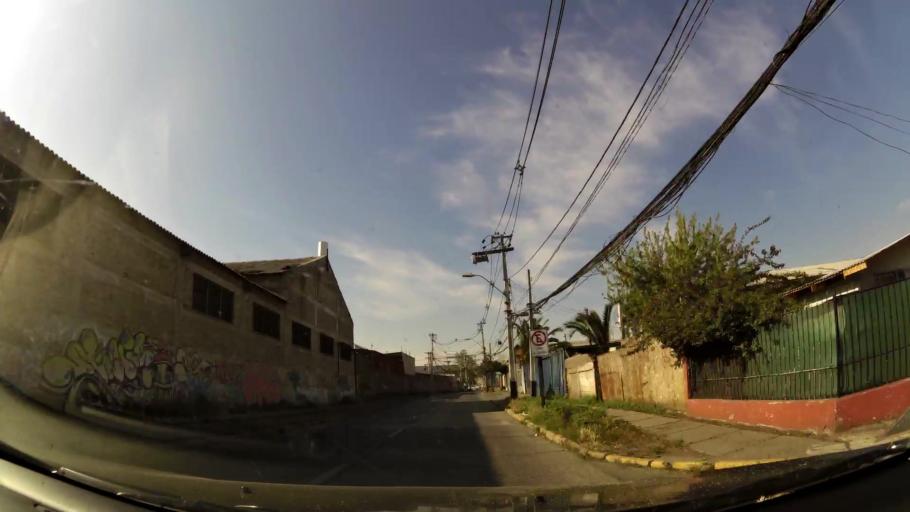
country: CL
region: Santiago Metropolitan
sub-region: Provincia de Santiago
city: Santiago
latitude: -33.4043
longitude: -70.6749
